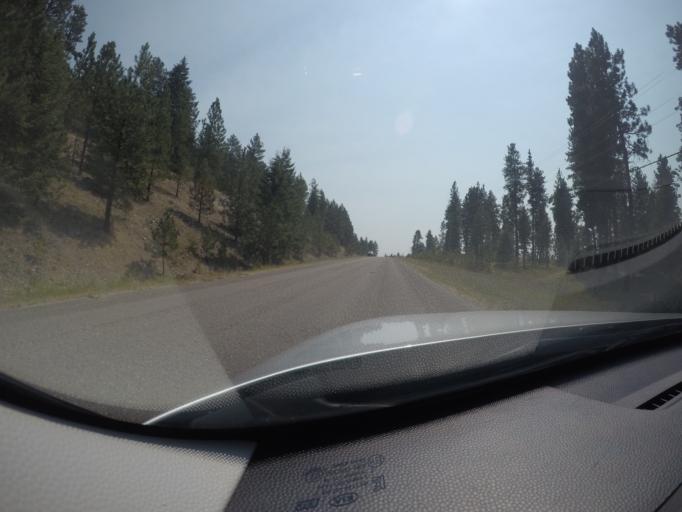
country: US
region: Montana
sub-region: Lake County
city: Polson
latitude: 47.7673
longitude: -114.1676
